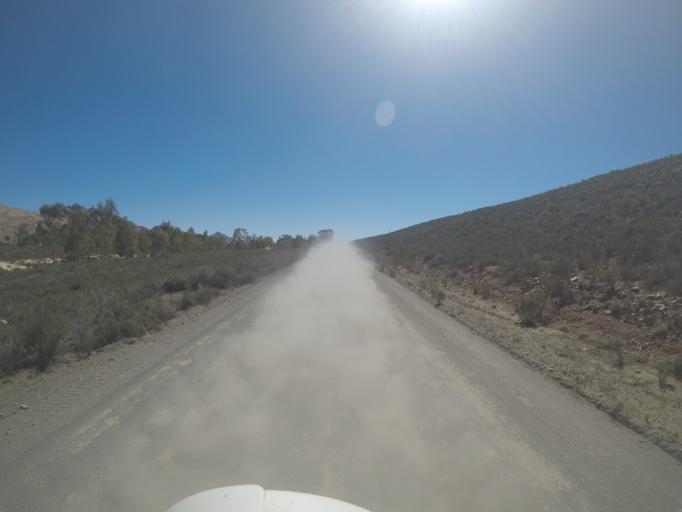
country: ZA
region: Western Cape
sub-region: Cape Winelands District Municipality
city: Ceres
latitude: -32.8160
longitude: 19.4519
